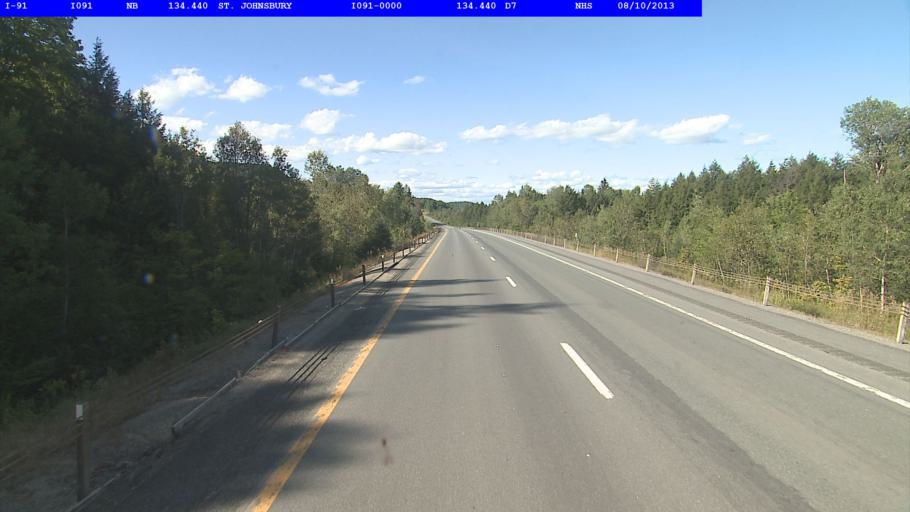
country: US
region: Vermont
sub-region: Caledonia County
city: Lyndon
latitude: 44.4807
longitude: -72.0223
